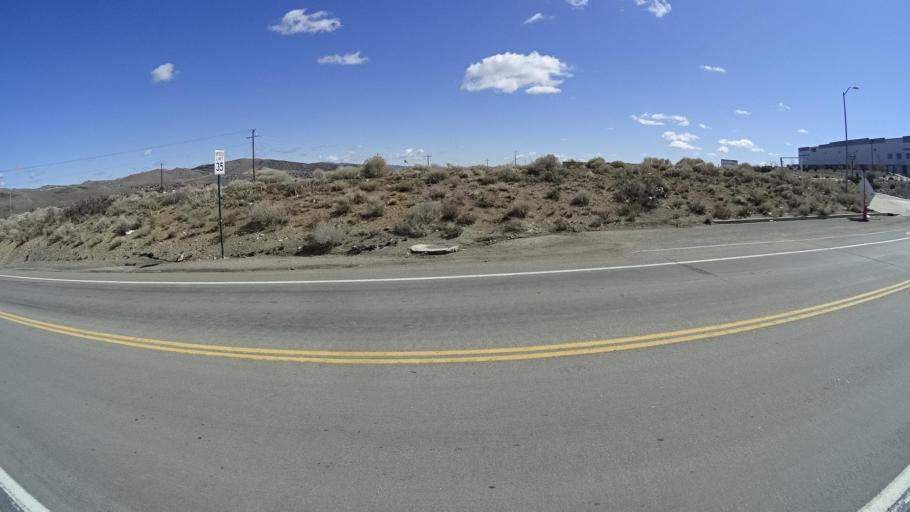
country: US
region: Nevada
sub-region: Washoe County
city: Golden Valley
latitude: 39.6083
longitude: -119.8530
